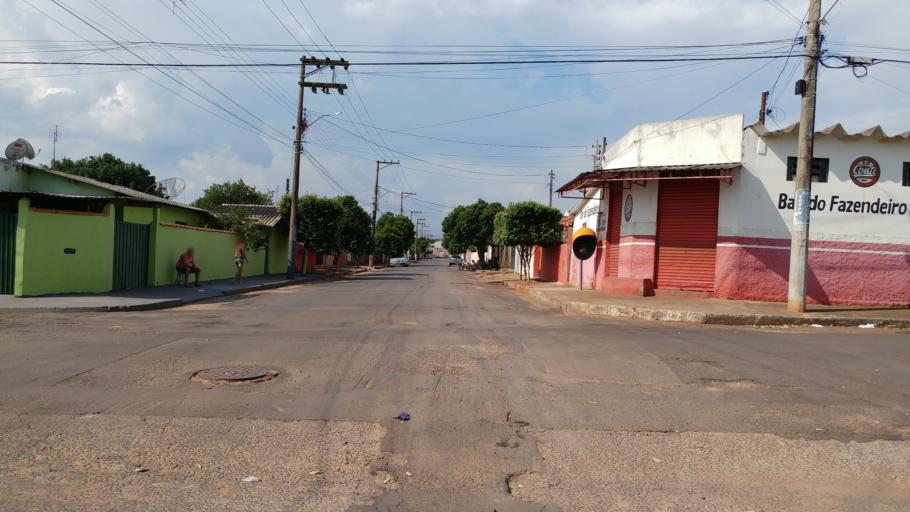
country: BR
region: Sao Paulo
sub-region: Paraguacu Paulista
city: Paraguacu Paulista
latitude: -22.4235
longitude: -50.5871
